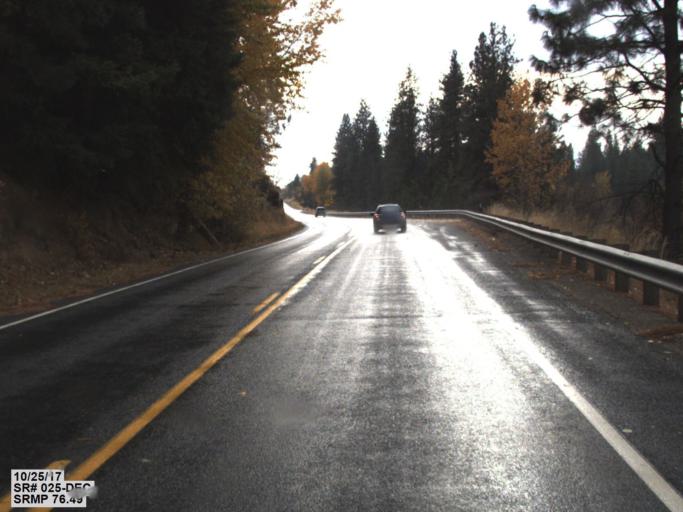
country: US
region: Washington
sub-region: Stevens County
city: Kettle Falls
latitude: 48.5608
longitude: -118.1198
